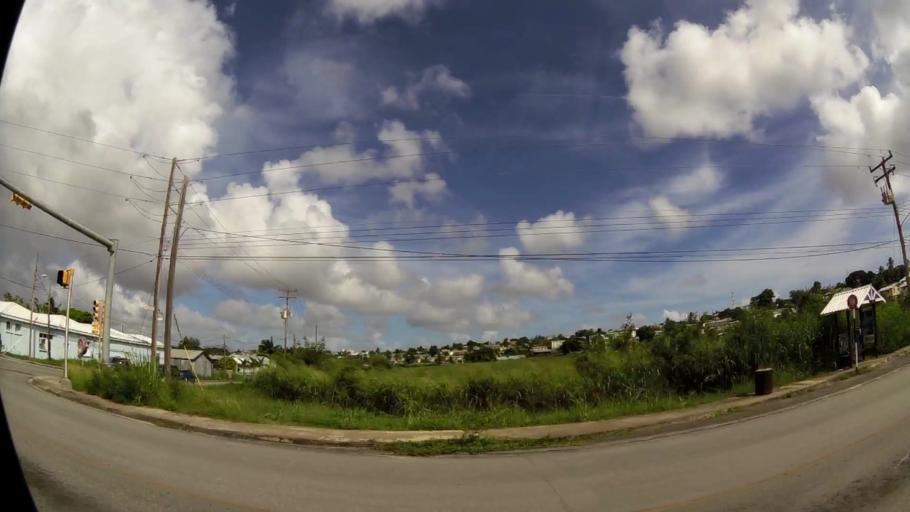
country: BB
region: Saint Michael
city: Bridgetown
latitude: 13.0984
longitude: -59.5928
